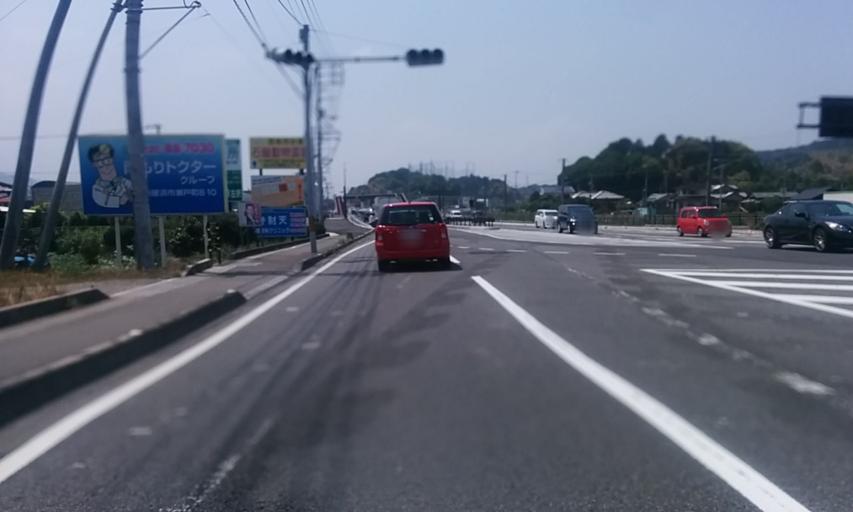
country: JP
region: Ehime
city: Niihama
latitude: 33.9283
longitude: 133.2677
